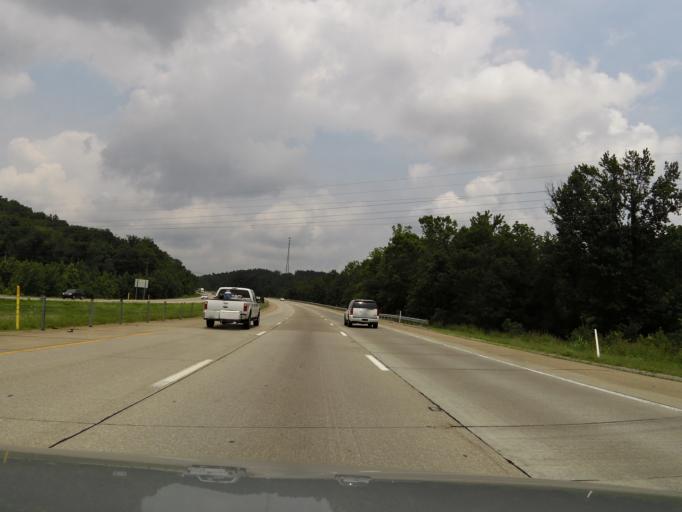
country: US
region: Kentucky
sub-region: Bullitt County
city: Shepherdsville
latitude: 37.9510
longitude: -85.6889
